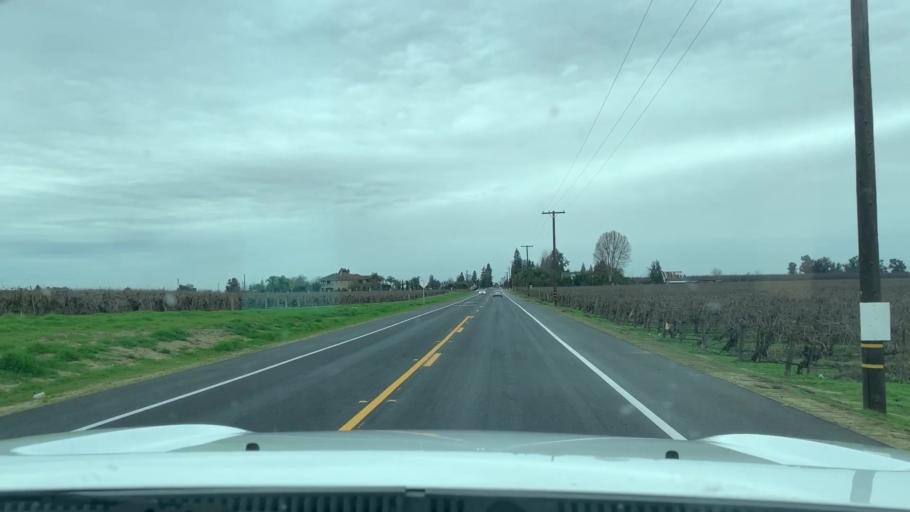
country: US
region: California
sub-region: Fresno County
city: Fowler
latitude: 36.5624
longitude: -119.6824
